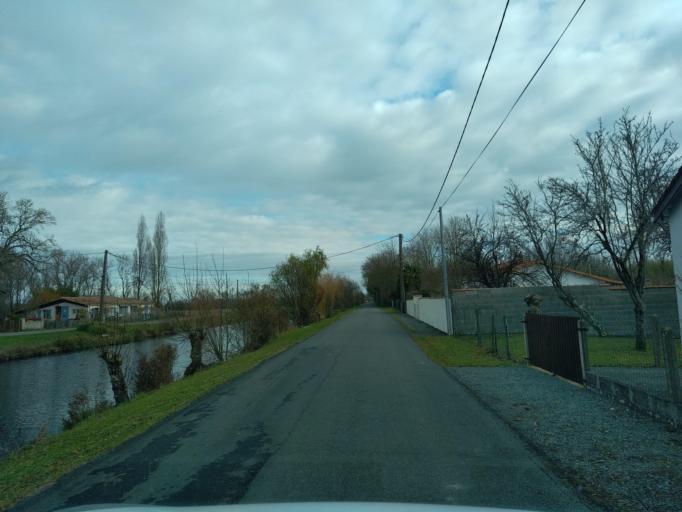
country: FR
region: Pays de la Loire
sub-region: Departement de la Vendee
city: Maillezais
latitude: 46.3173
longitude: -0.7623
